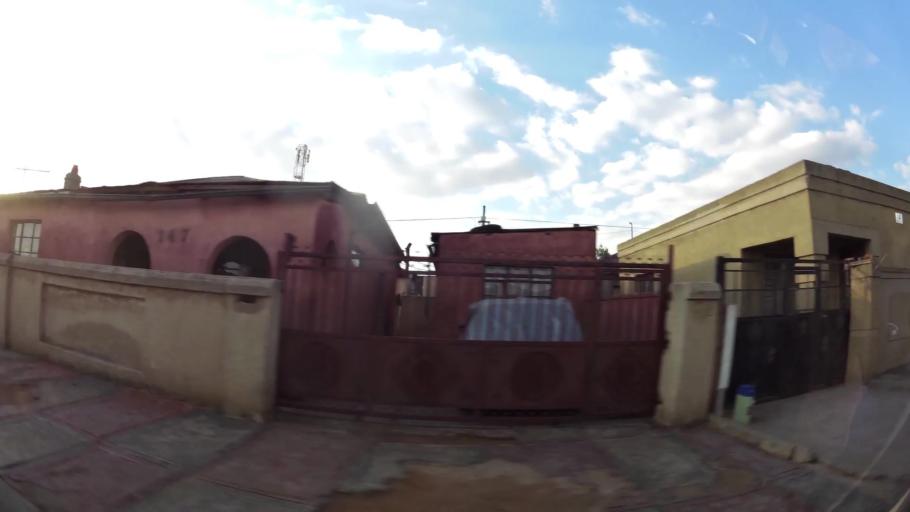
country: ZA
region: Gauteng
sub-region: West Rand District Municipality
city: Krugersdorp
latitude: -26.0725
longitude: 27.7595
